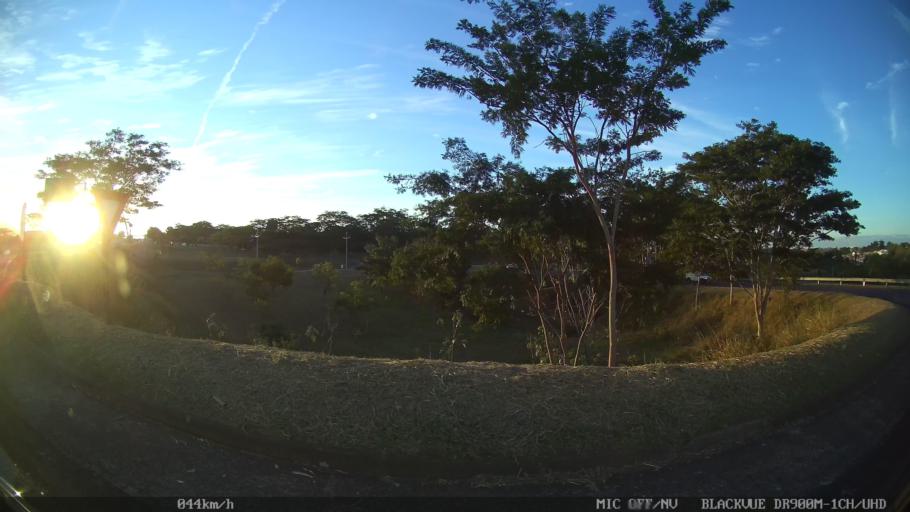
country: BR
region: Sao Paulo
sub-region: Catanduva
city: Catanduva
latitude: -21.1602
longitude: -48.9851
